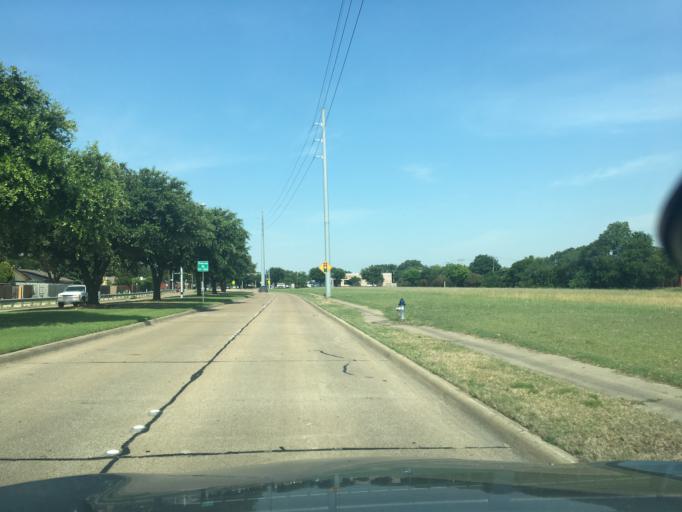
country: US
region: Texas
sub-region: Dallas County
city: Garland
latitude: 32.9608
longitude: -96.6717
